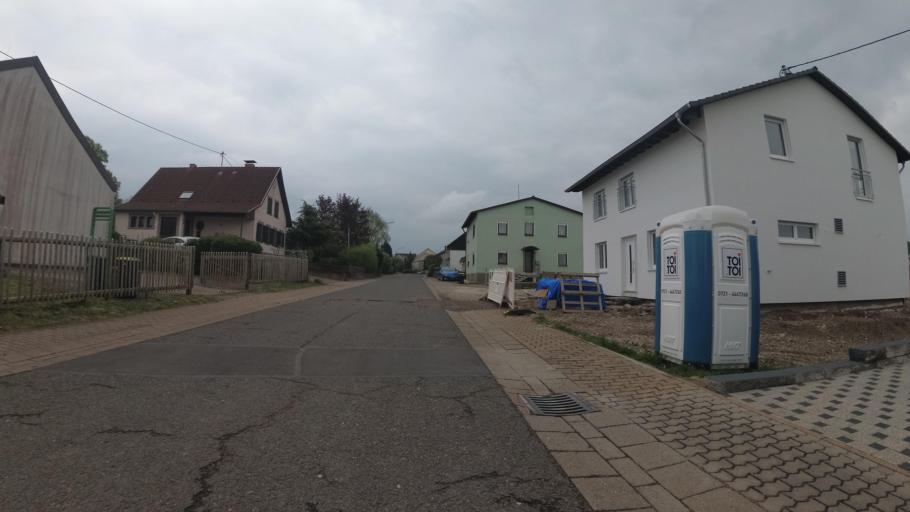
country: FR
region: Lorraine
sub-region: Departement de la Moselle
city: Merten
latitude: 49.2993
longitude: 6.6552
